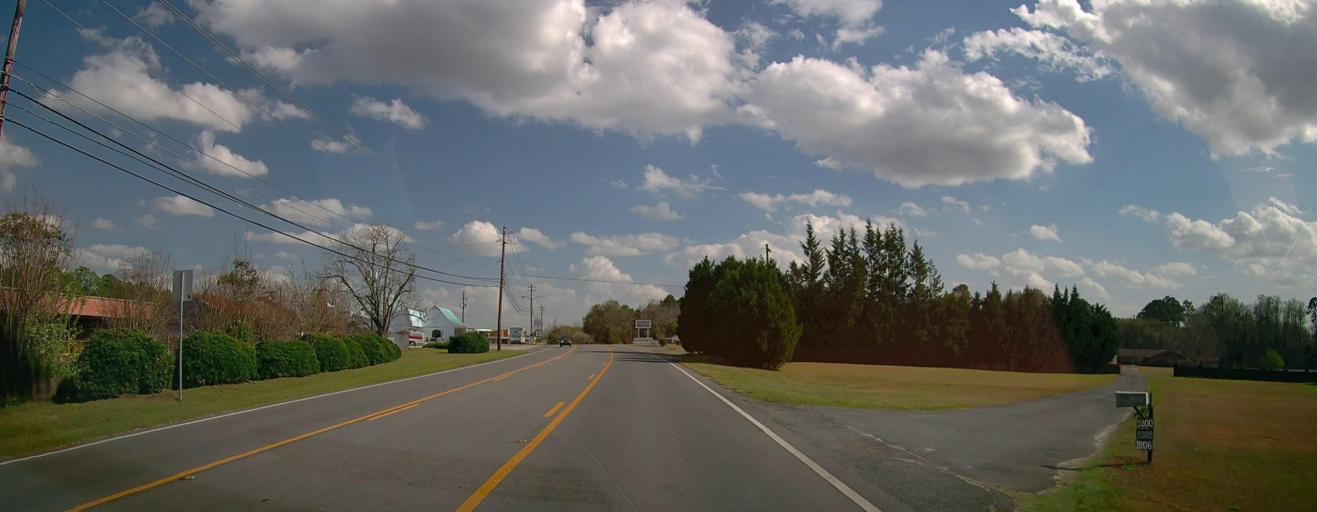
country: US
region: Georgia
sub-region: Dodge County
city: Eastman
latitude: 32.1840
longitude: -83.1696
